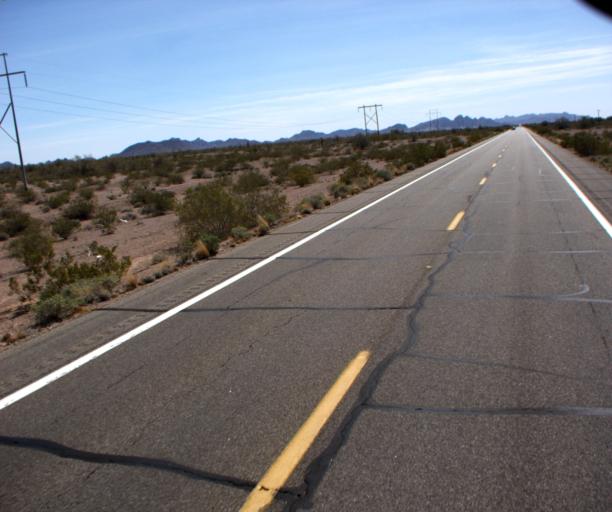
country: US
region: Arizona
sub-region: La Paz County
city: Quartzsite
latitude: 33.4080
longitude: -114.2172
